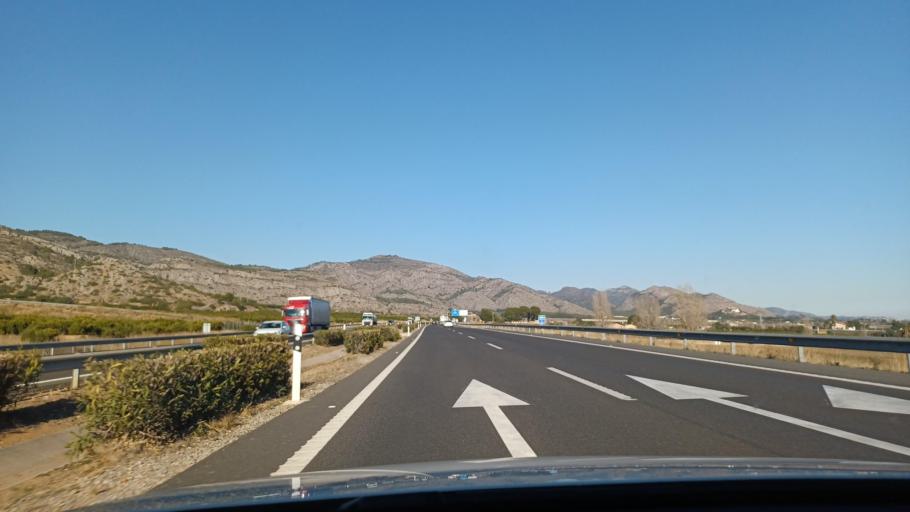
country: ES
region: Valencia
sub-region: Provincia de Castello
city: Castello de la Plana
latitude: 40.0197
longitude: -0.0385
